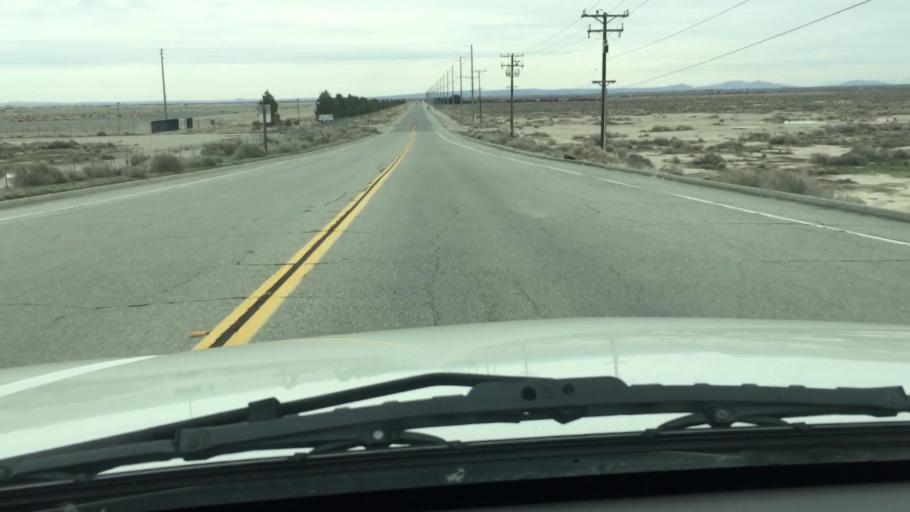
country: US
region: California
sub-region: Los Angeles County
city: Lancaster
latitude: 34.7769
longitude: -118.1685
